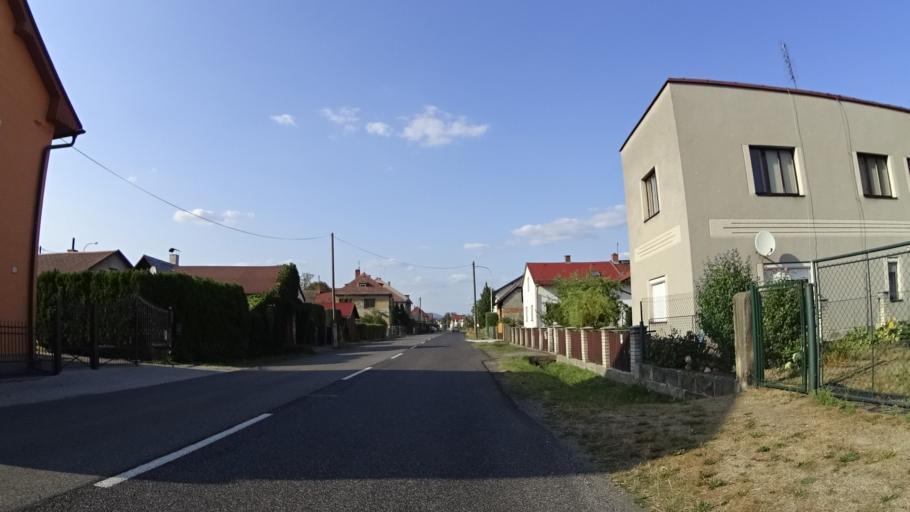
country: CZ
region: Central Bohemia
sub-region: Okres Mlada Boleslav
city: Zd'ar
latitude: 50.5537
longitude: 15.0680
